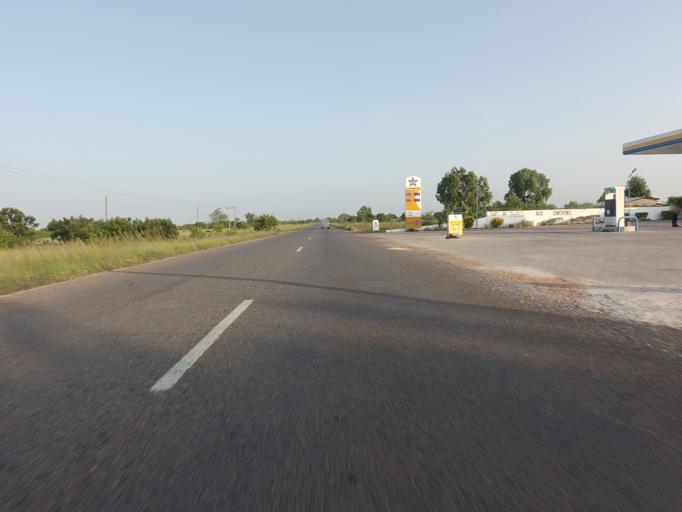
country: GH
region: Volta
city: Anloga
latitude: 6.0050
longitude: 0.6697
